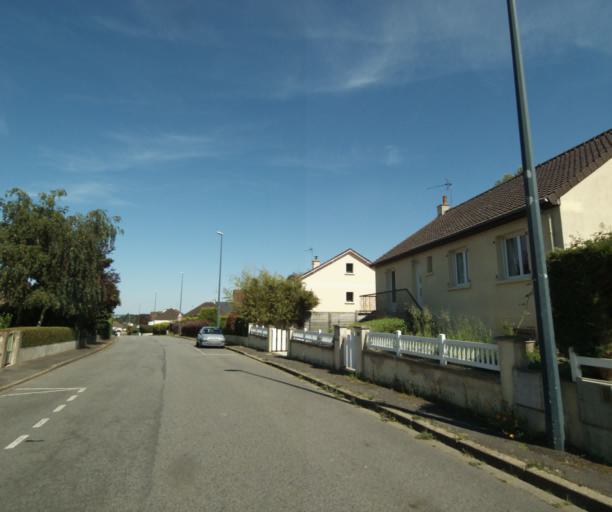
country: FR
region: Pays de la Loire
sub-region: Departement de la Mayenne
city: Laval
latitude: 48.0581
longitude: -0.7942
